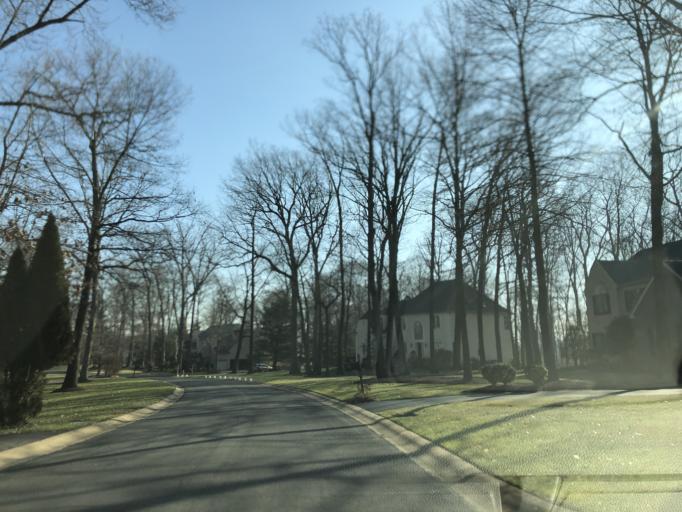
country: US
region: Pennsylvania
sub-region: Chester County
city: Downingtown
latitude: 39.9872
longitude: -75.6975
